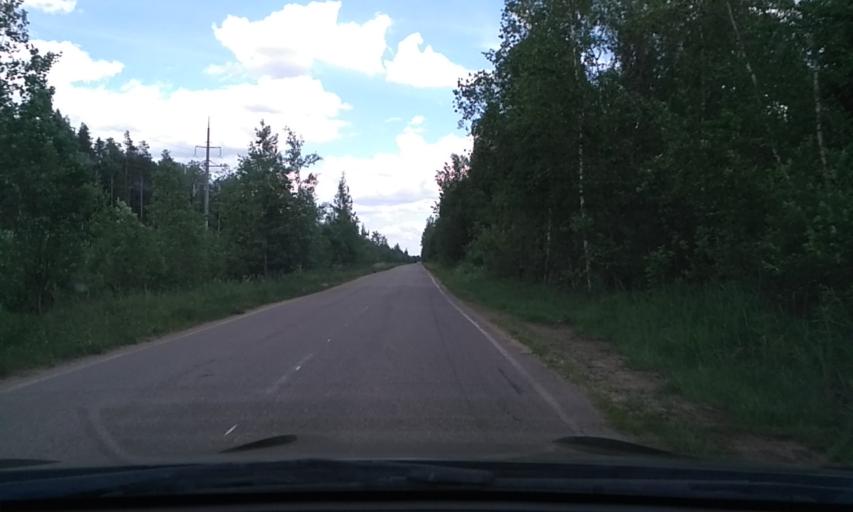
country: RU
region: Leningrad
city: Otradnoye
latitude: 59.8203
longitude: 30.7996
